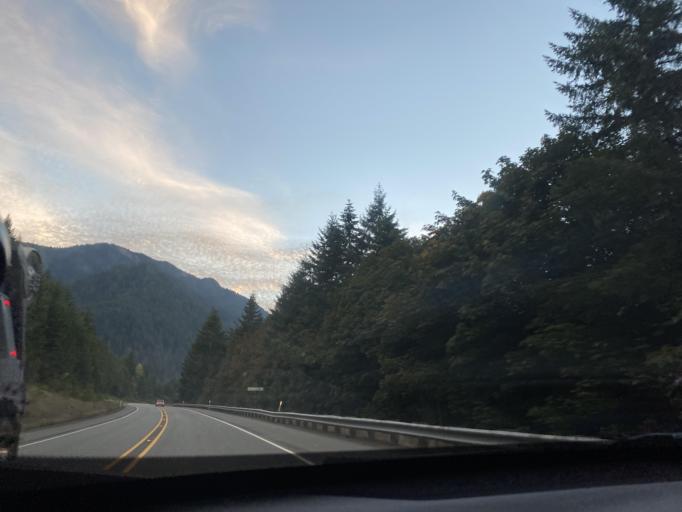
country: US
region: Washington
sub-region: Clallam County
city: Port Angeles
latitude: 48.0656
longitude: -123.5893
